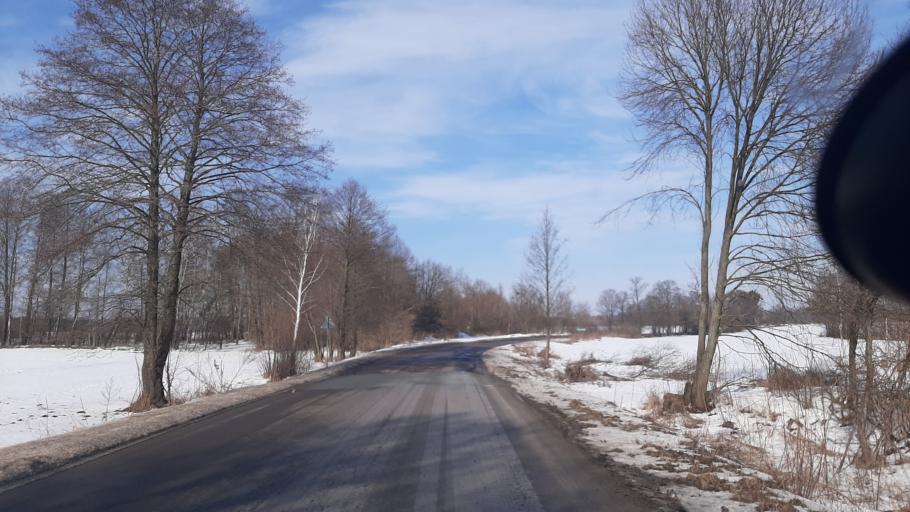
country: PL
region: Lublin Voivodeship
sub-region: Powiat pulawski
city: Kurow
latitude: 51.4146
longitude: 22.2018
